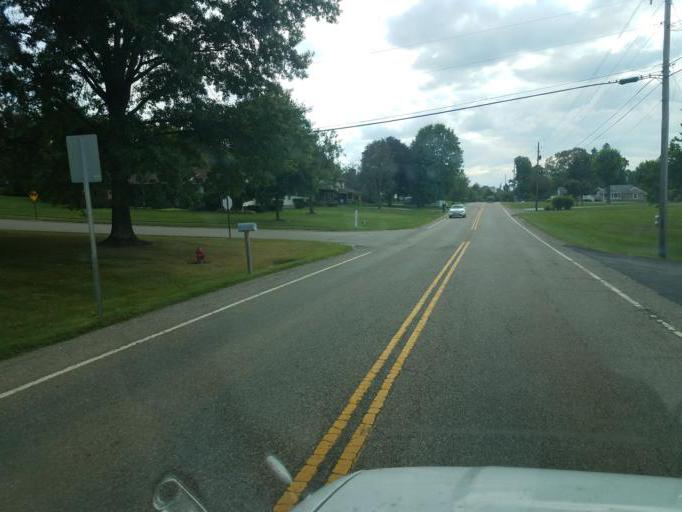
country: US
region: Ohio
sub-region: Stark County
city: Louisville
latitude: 40.8263
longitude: -81.2649
